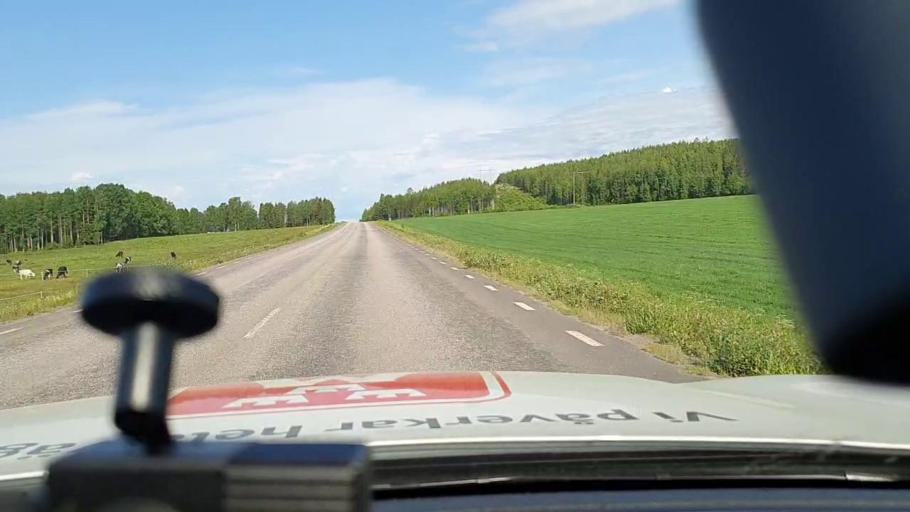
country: SE
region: Norrbotten
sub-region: Bodens Kommun
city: Boden
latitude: 65.9126
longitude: 21.3450
